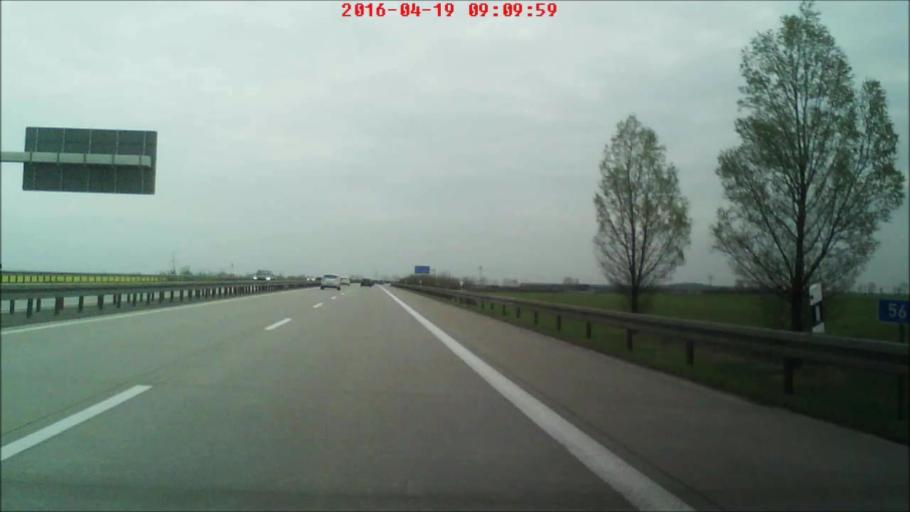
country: DE
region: Thuringia
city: Noda
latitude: 51.0346
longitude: 11.0102
